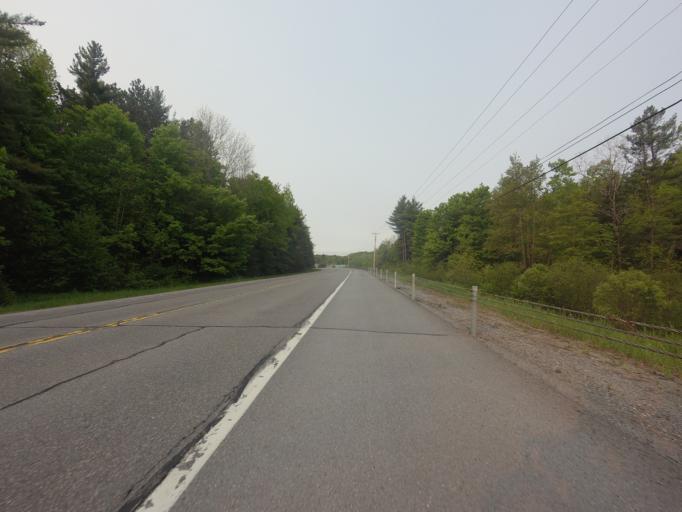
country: US
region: New York
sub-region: Jefferson County
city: Carthage
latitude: 44.1041
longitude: -75.4104
